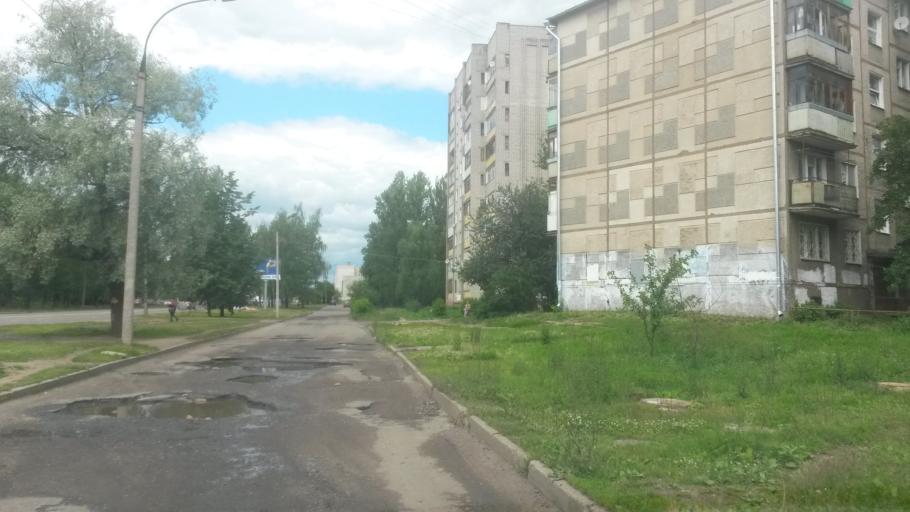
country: RU
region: Jaroslavl
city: Yaroslavl
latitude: 57.6829
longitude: 39.7724
